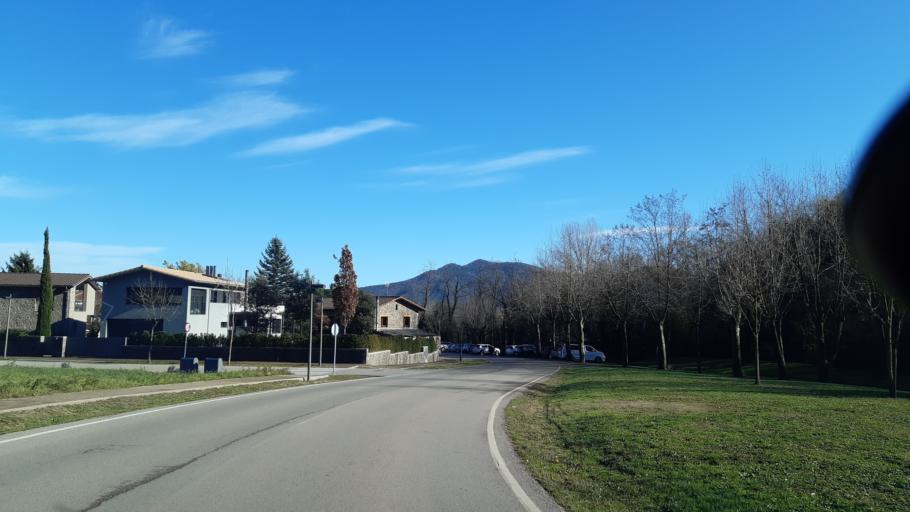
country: ES
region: Catalonia
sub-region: Provincia de Girona
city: Bas
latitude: 42.1497
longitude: 2.4164
